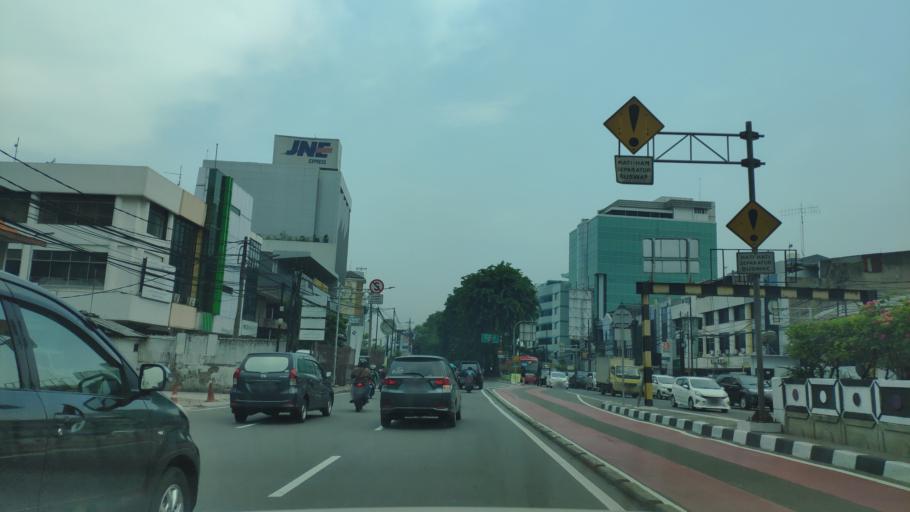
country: ID
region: Jakarta Raya
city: Jakarta
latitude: -6.1789
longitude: 106.7971
